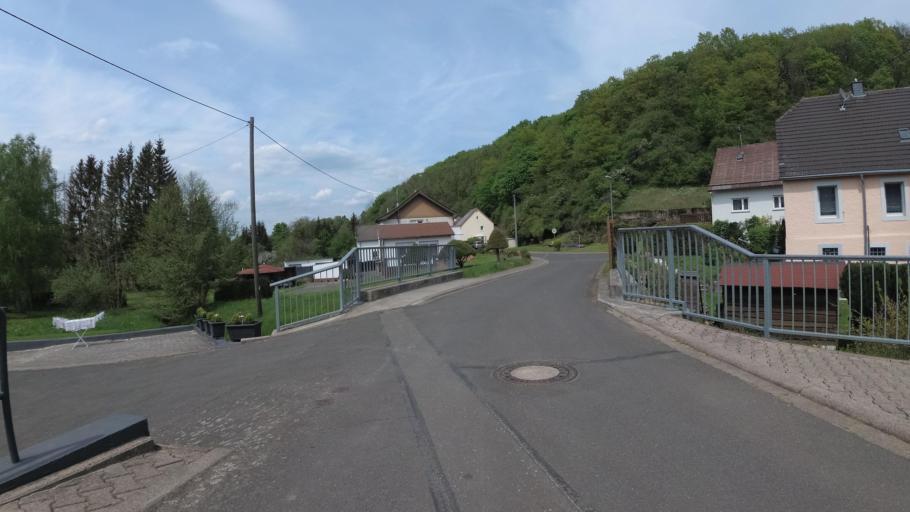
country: DE
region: Rheinland-Pfalz
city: Fohren-Linden
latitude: 49.5751
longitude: 7.2958
